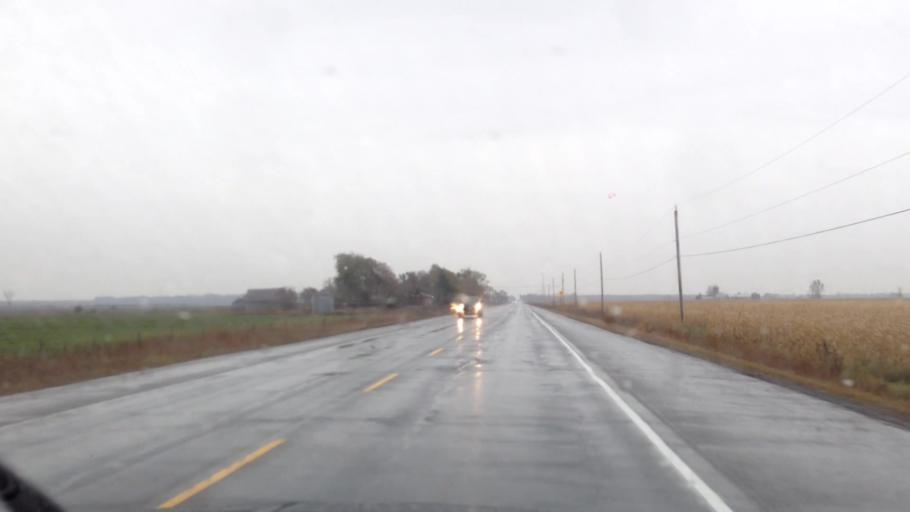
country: CA
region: Ontario
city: Clarence-Rockland
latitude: 45.4617
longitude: -75.4303
